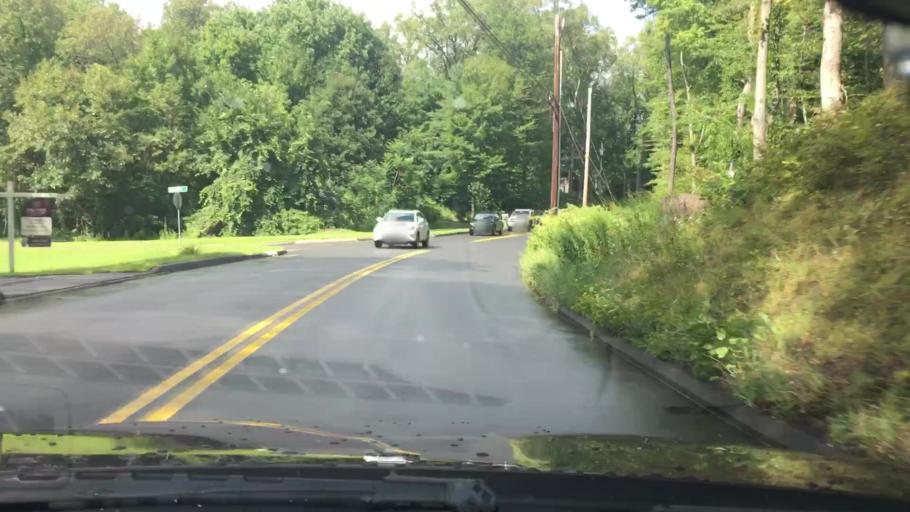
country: US
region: Connecticut
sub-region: Hartford County
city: Manchester
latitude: 41.7251
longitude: -72.5369
